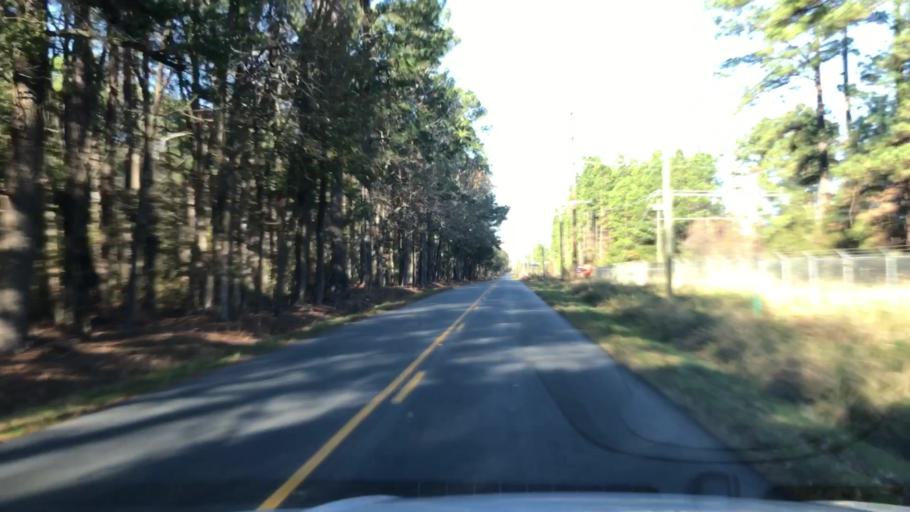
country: US
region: South Carolina
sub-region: Berkeley County
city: Ladson
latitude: 32.9873
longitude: -80.1127
